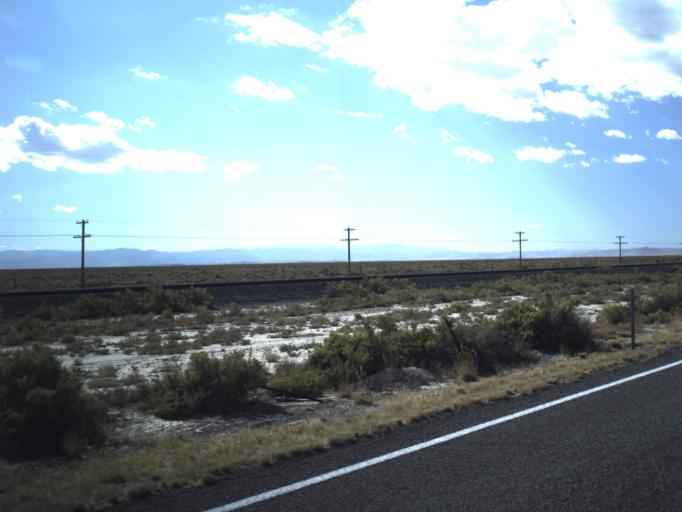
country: US
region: Utah
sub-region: Millard County
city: Delta
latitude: 39.0943
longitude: -112.7499
